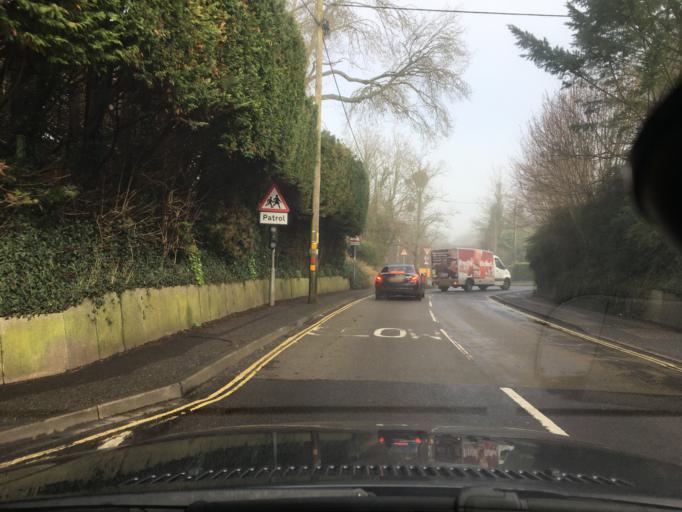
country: GB
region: England
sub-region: Hampshire
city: Old Basing
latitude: 51.2703
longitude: -1.0447
